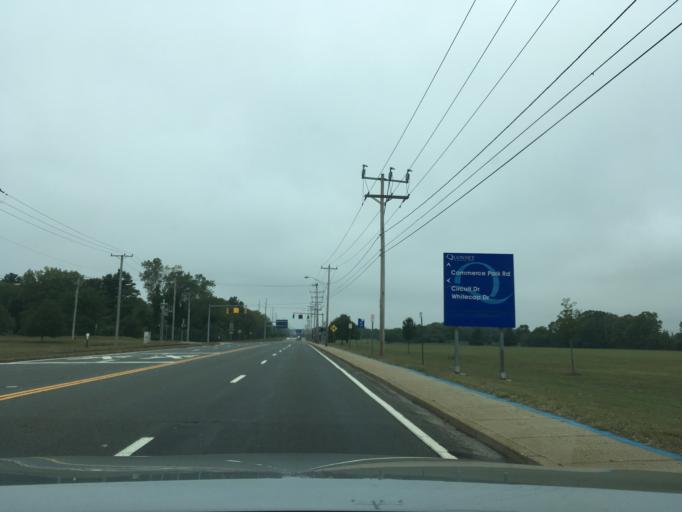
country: US
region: Rhode Island
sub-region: Washington County
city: North Kingstown
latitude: 41.5928
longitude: -71.4308
